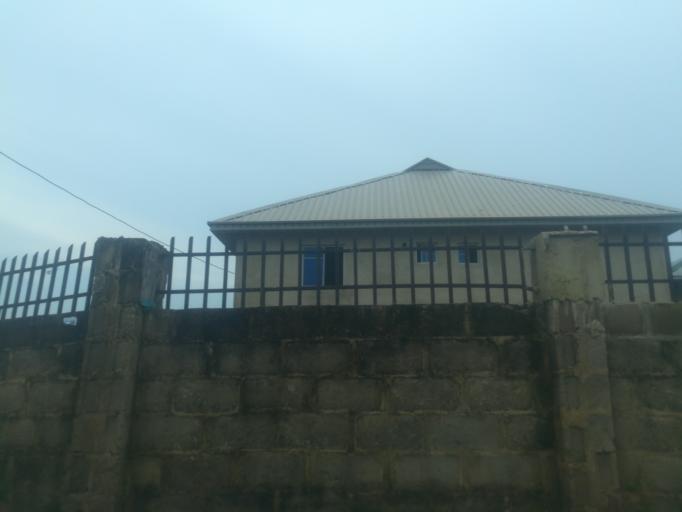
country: NG
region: Oyo
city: Ibadan
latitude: 7.3707
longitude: 3.8283
